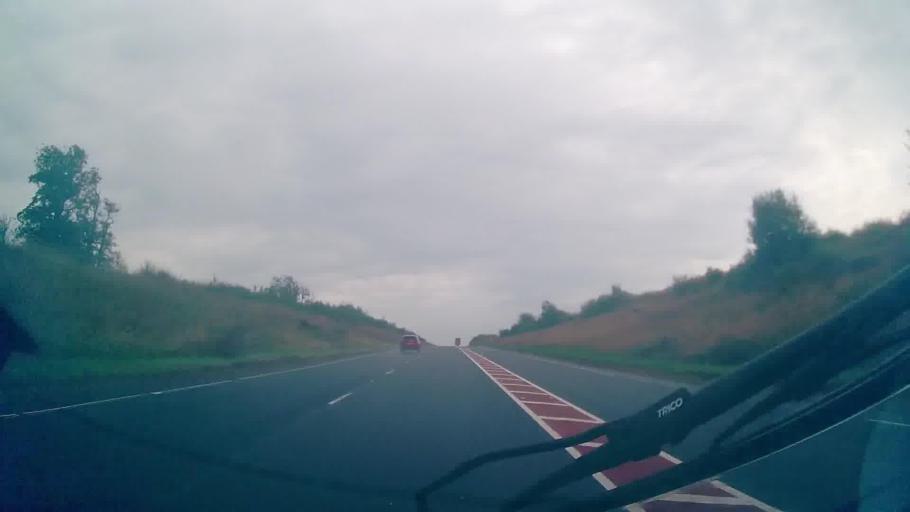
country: GB
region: Scotland
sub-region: Dumfries and Galloway
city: Lockerbie
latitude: 55.0251
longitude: -3.3811
